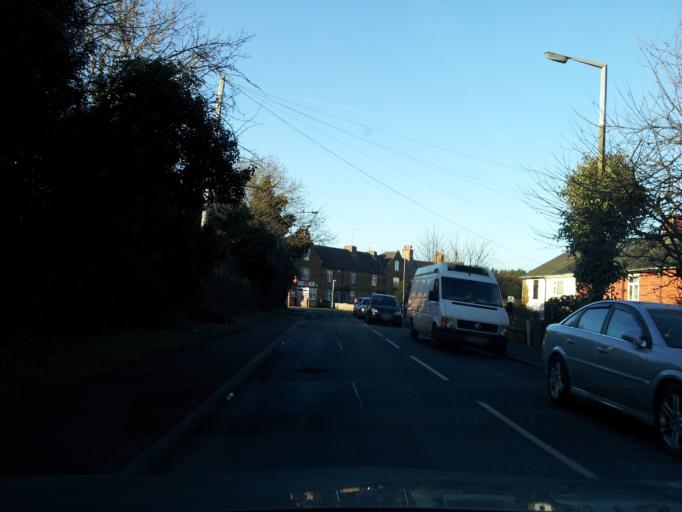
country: GB
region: England
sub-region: Northamptonshire
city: Northampton
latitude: 52.2586
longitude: -0.9530
